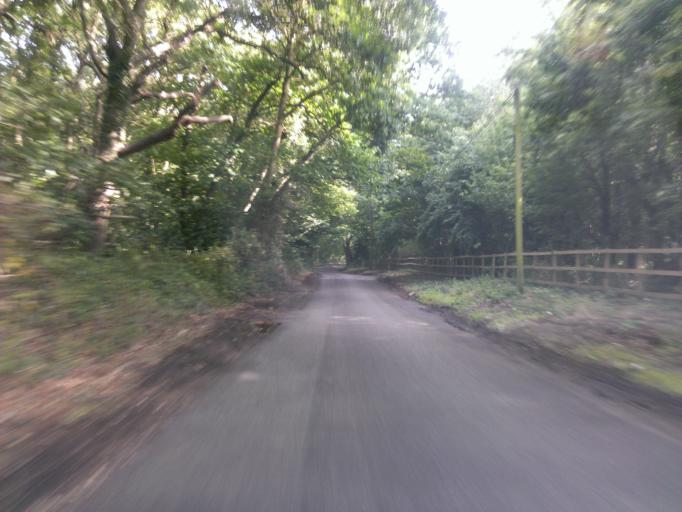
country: GB
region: England
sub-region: Essex
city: Saint Osyth
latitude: 51.8326
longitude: 1.1032
